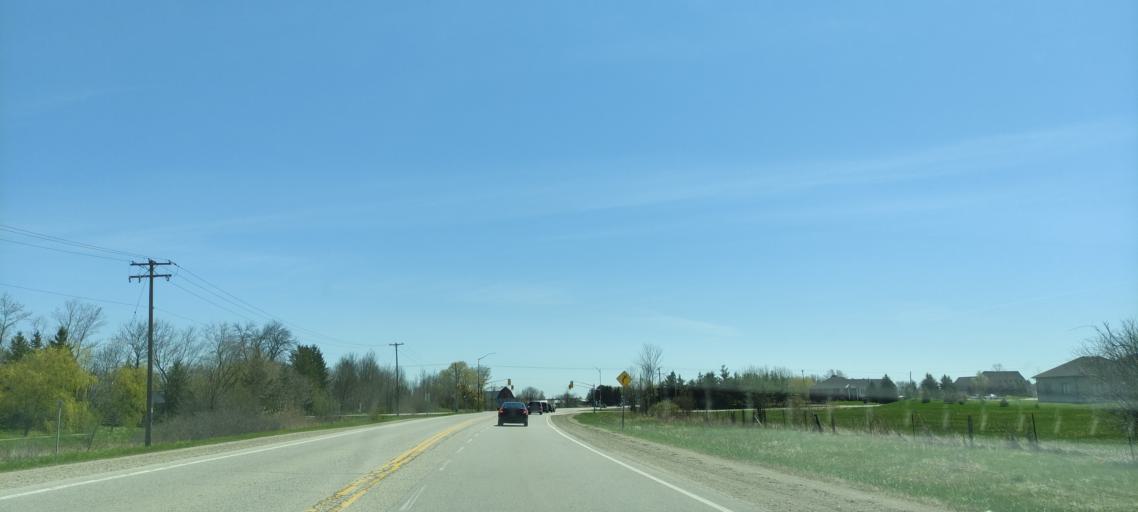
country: CA
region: Ontario
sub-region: Wellington County
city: Guelph
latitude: 43.5754
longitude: -80.3686
